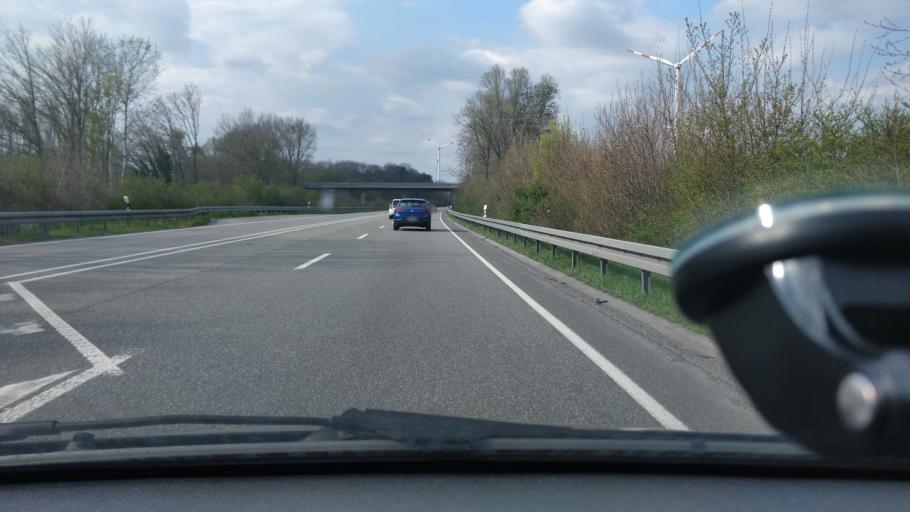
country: DE
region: North Rhine-Westphalia
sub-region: Regierungsbezirk Dusseldorf
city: Hamminkeln
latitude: 51.7836
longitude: 6.5783
